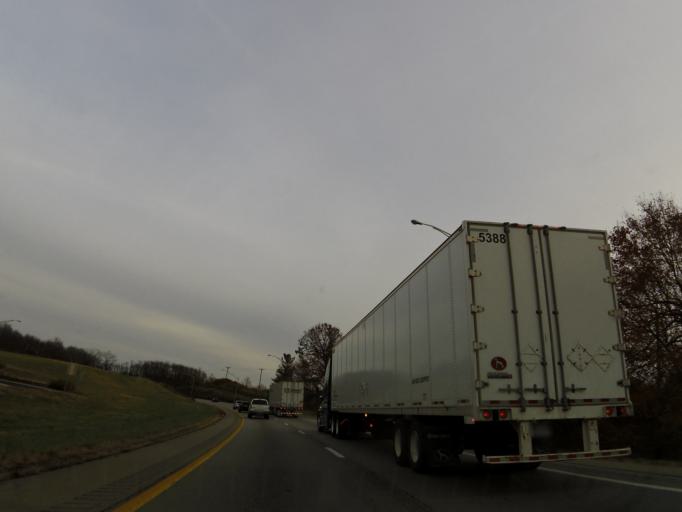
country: US
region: Kentucky
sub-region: Fayette County
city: Lexington-Fayette
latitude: 38.1132
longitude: -84.5242
